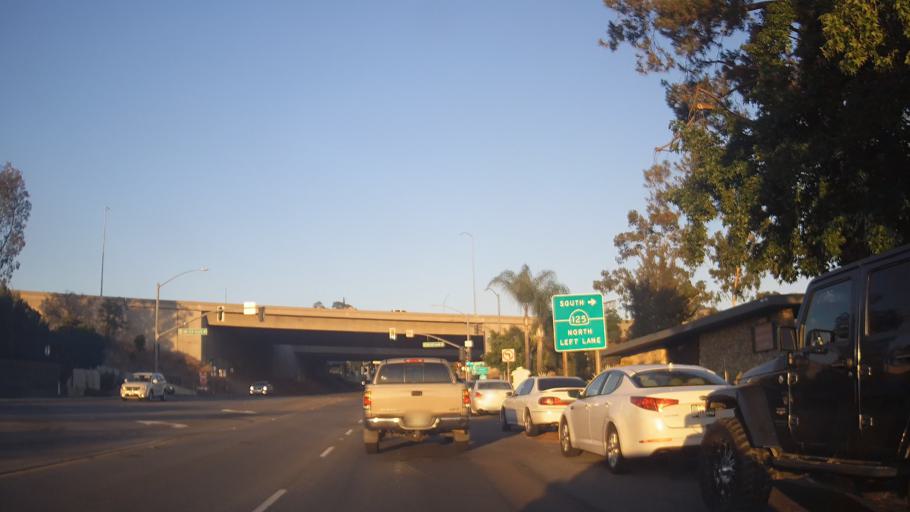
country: US
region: California
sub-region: San Diego County
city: La Mesa
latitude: 32.7734
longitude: -117.0036
